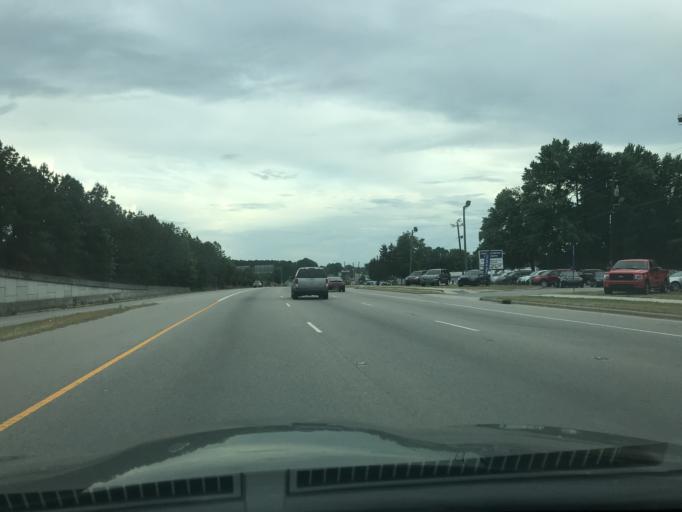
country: US
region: North Carolina
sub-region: Wake County
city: Raleigh
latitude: 35.8397
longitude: -78.5802
